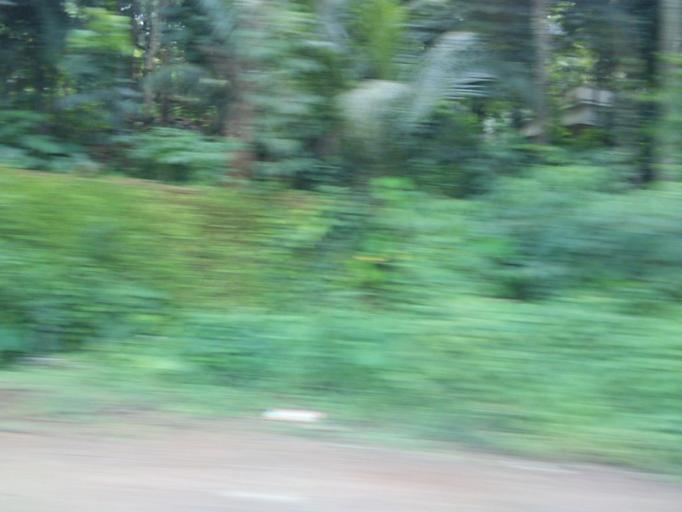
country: IN
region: Kerala
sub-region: Kozhikode
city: Kunnamangalam
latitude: 11.3054
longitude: 75.8865
